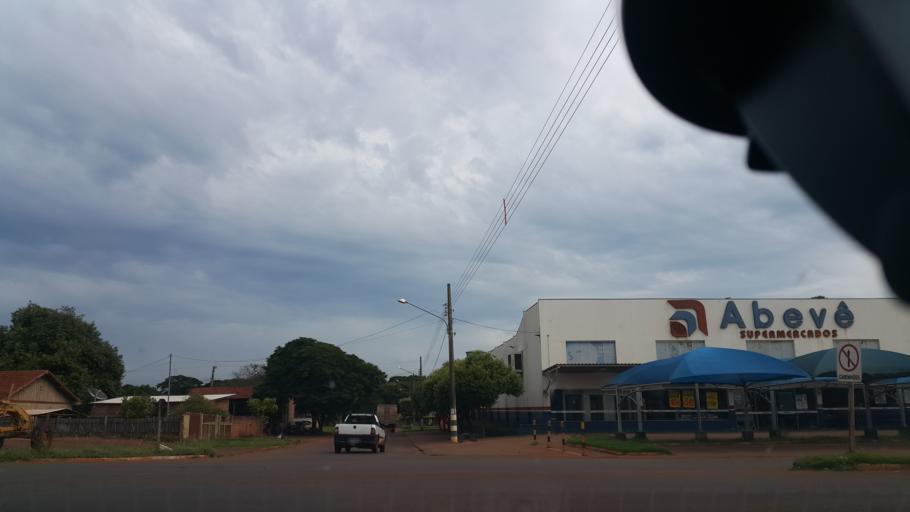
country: BR
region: Mato Grosso do Sul
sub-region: Dourados
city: Dourados
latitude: -22.0822
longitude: -54.7938
